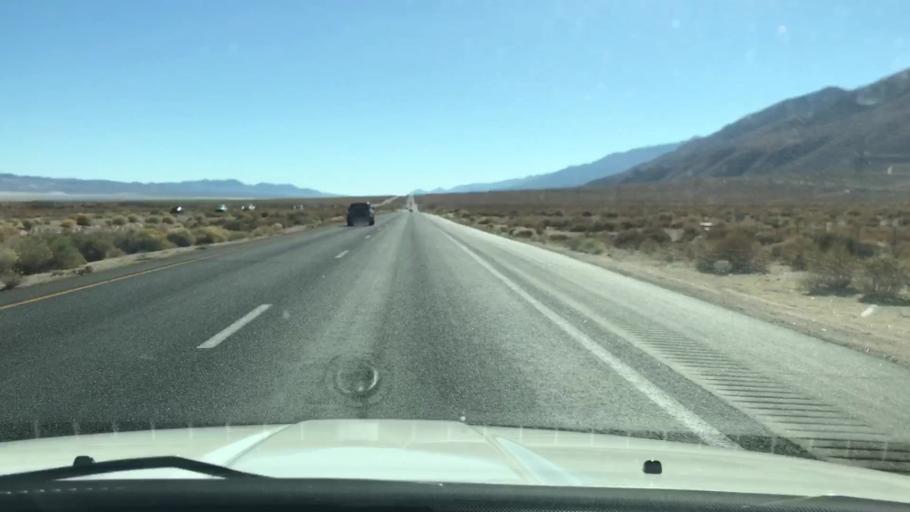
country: US
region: California
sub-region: Inyo County
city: Lone Pine
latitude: 36.4163
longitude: -118.0290
